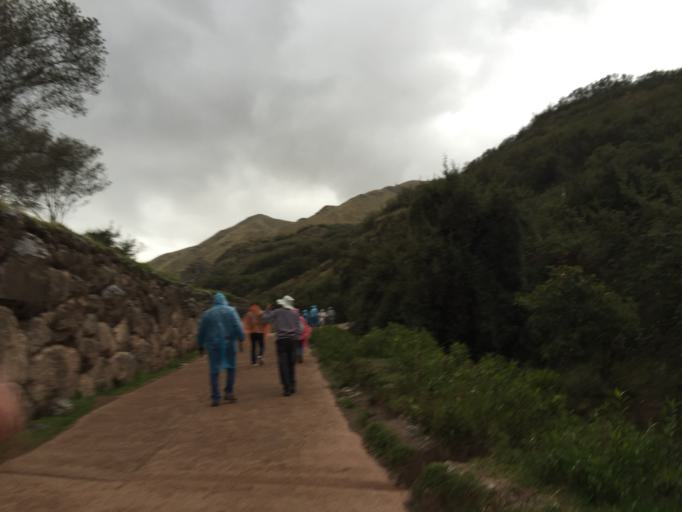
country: PE
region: Cusco
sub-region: Provincia de Cusco
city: Cusco
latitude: -13.4800
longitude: -71.9658
